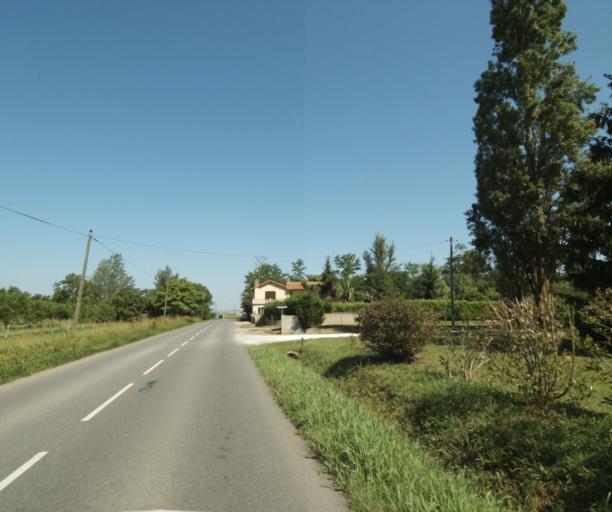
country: FR
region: Midi-Pyrenees
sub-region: Departement du Tarn-et-Garonne
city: Montbeton
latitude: 44.0423
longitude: 1.2949
